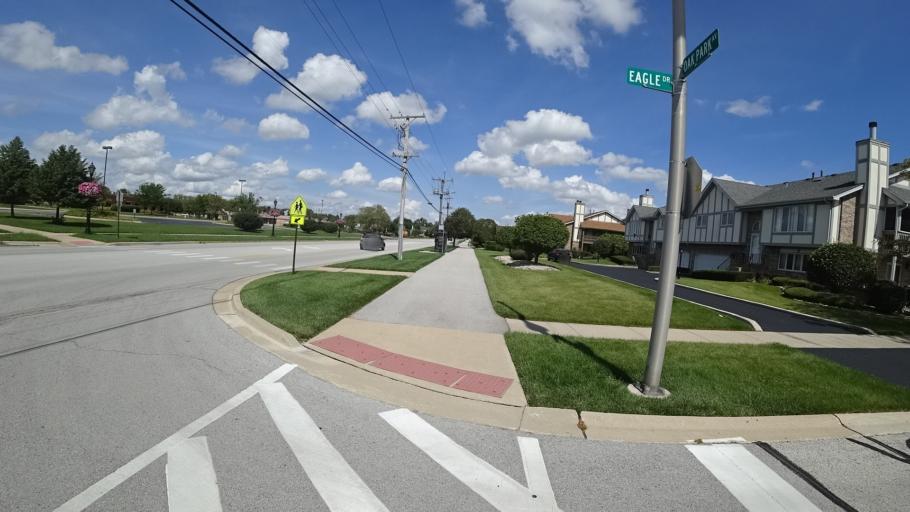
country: US
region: Illinois
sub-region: Cook County
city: Tinley Park
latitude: 41.5614
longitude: -87.7837
